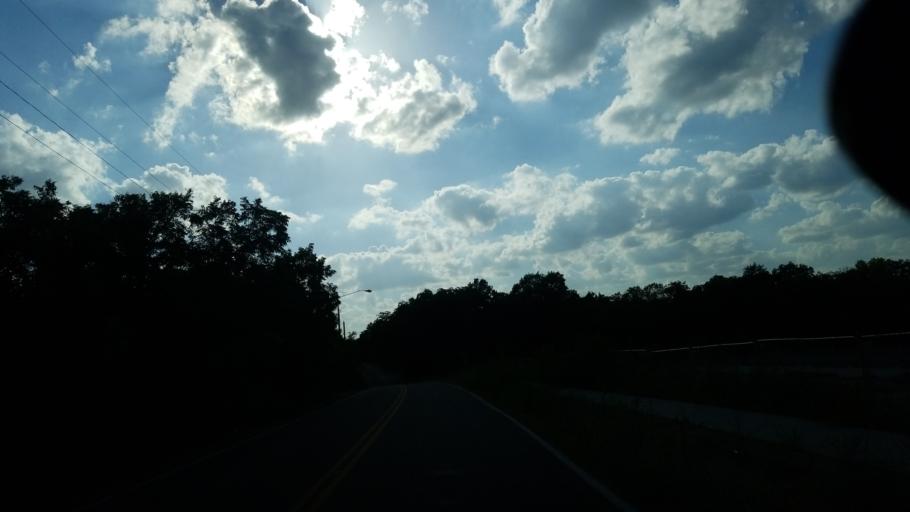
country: US
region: Texas
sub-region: Dallas County
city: Dallas
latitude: 32.7792
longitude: -96.7083
